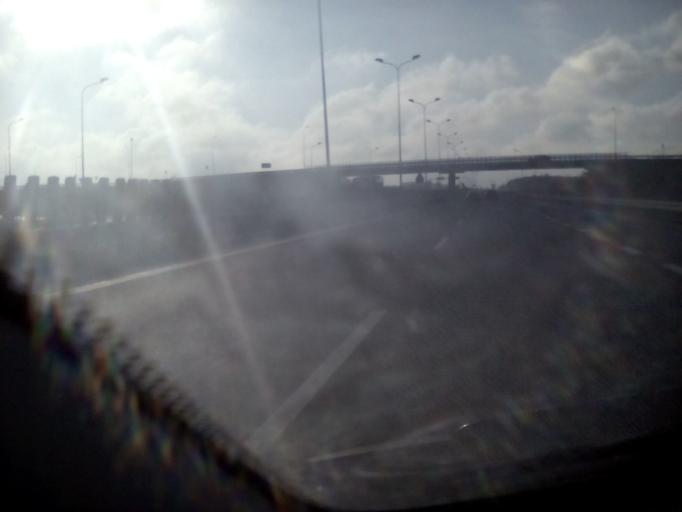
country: PL
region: Masovian Voivodeship
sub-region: Powiat grojecki
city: Goszczyn
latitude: 51.7613
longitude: 20.9037
